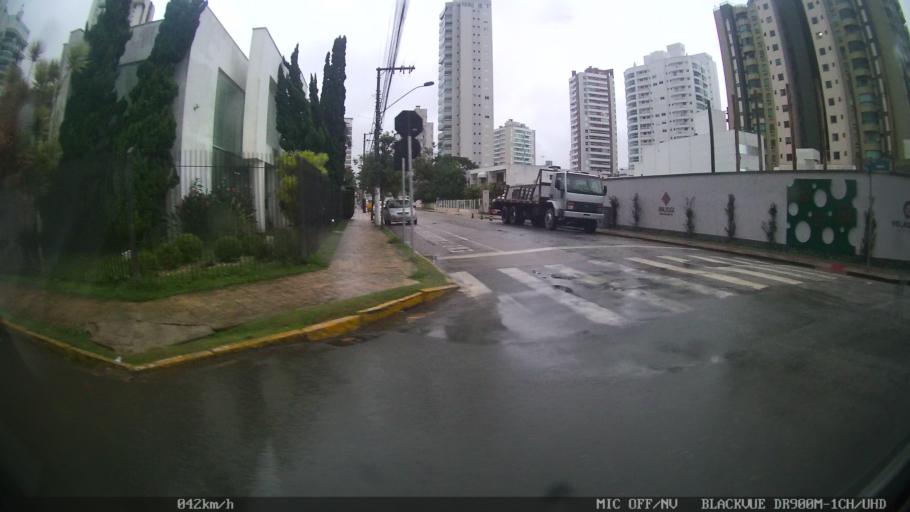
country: BR
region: Santa Catarina
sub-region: Itajai
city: Itajai
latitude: -26.9127
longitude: -48.6544
